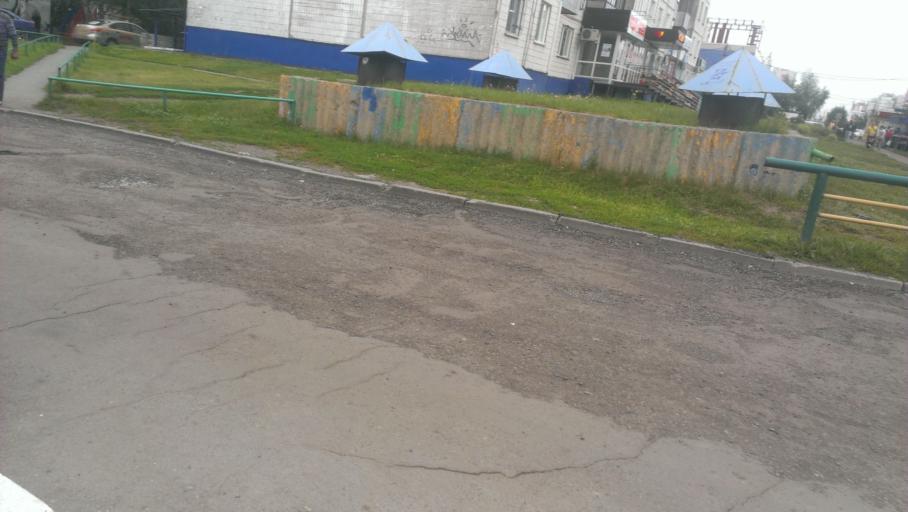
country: RU
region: Altai Krai
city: Novosilikatnyy
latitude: 53.3358
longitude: 83.6744
